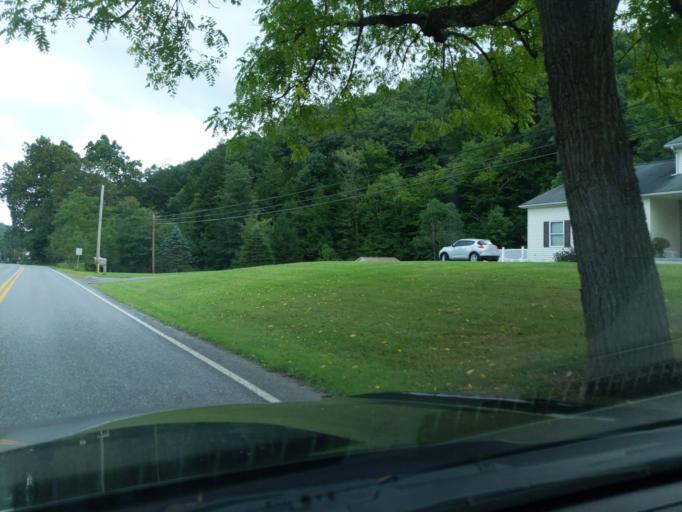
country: US
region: Pennsylvania
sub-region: Blair County
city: Duncansville
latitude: 40.3798
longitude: -78.4826
